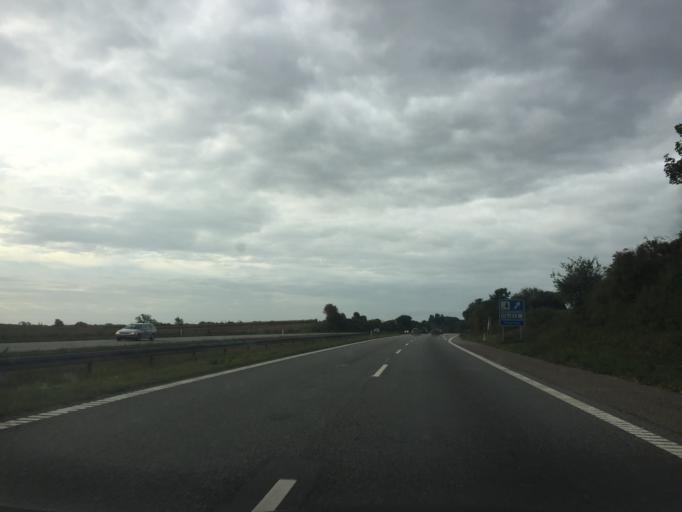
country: DK
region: Zealand
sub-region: Faxe Kommune
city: Haslev
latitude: 55.3302
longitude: 12.0385
